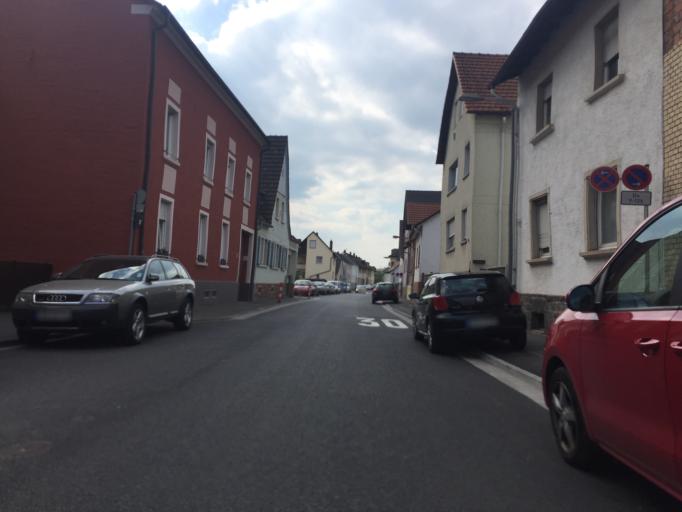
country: DE
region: Bavaria
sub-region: Regierungsbezirk Unterfranken
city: Glattbach
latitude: 49.9901
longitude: 9.1399
